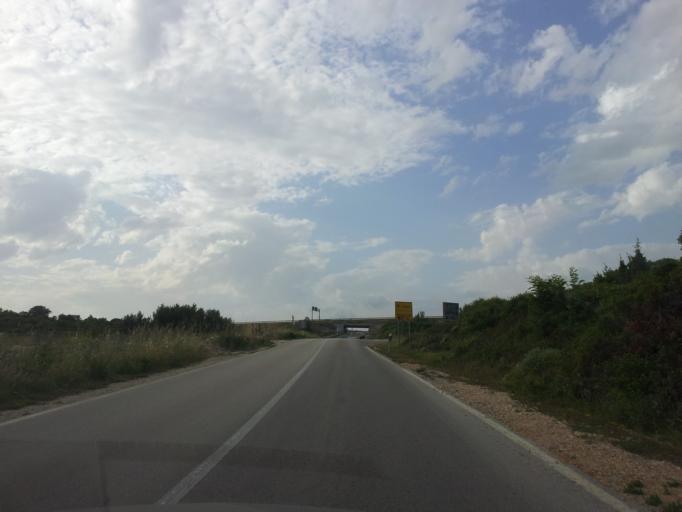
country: HR
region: Zadarska
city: Sukosan
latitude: 44.0683
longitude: 15.3404
